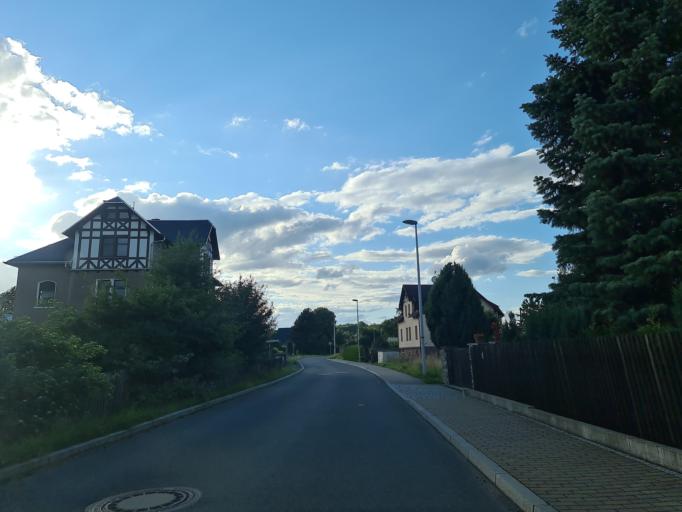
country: DE
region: Saxony
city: Syrau
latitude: 50.5254
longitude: 12.0905
